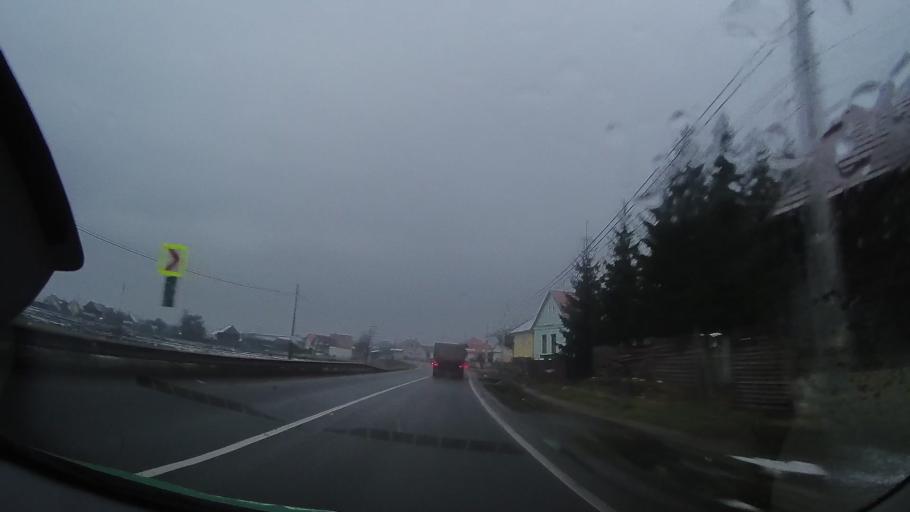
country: RO
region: Harghita
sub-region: Comuna Lazarea
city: Lazarea
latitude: 46.7532
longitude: 25.5194
